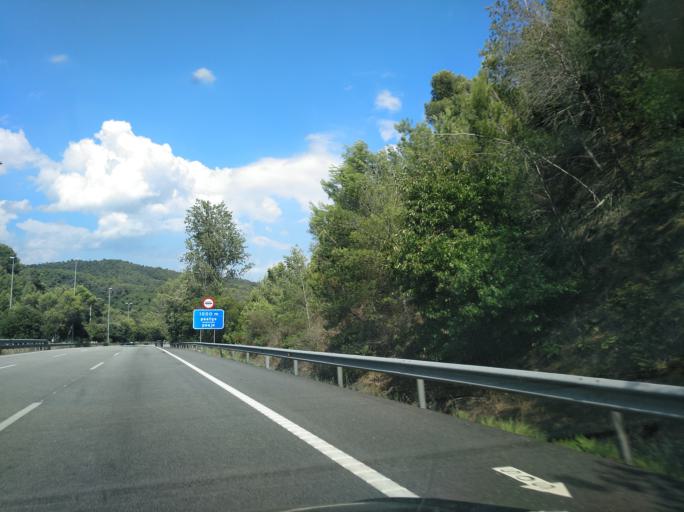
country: ES
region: Catalonia
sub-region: Provincia de Barcelona
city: Pineda de Mar
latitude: 41.6504
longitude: 2.6851
